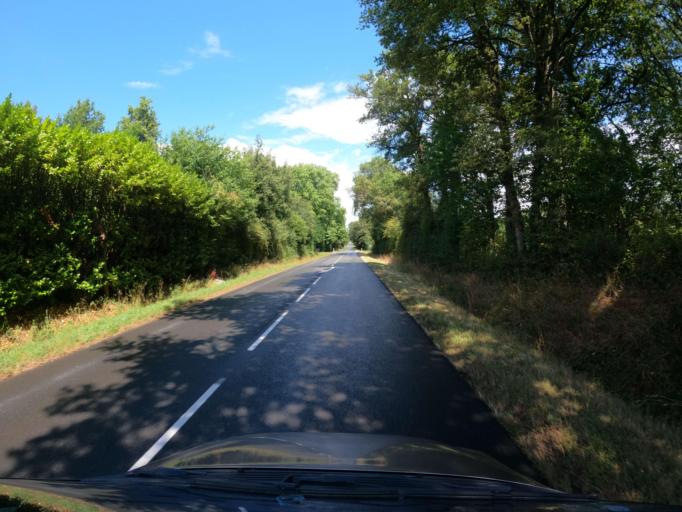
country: FR
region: Pays de la Loire
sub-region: Departement de Maine-et-Loire
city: Champigne
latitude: 47.6316
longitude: -0.5806
